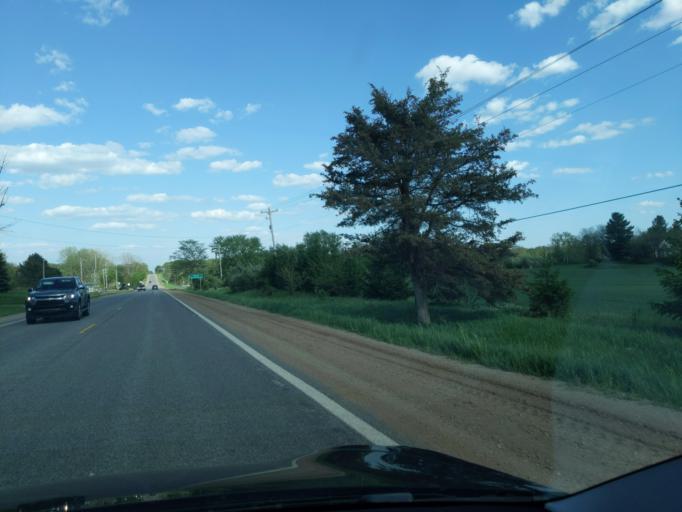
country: US
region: Michigan
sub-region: Ionia County
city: Portland
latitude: 42.7556
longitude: -84.9637
